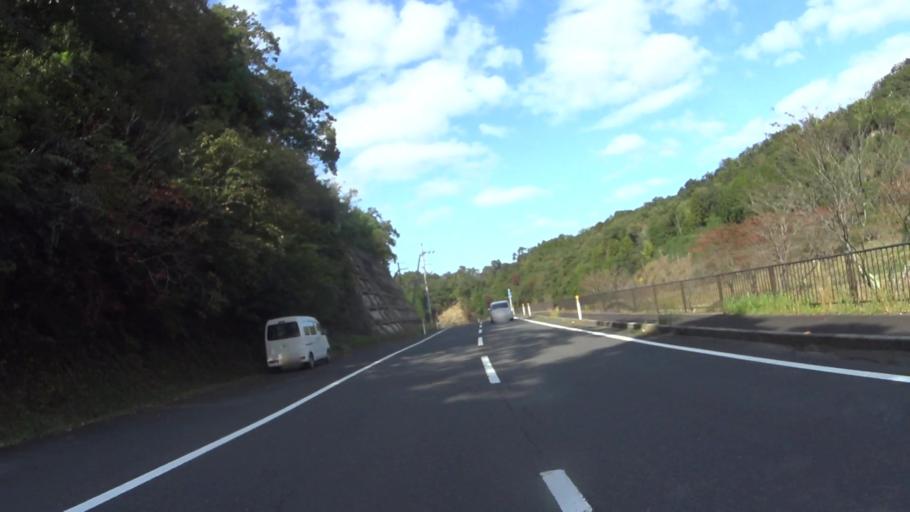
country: JP
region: Hyogo
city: Toyooka
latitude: 35.5624
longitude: 134.9782
